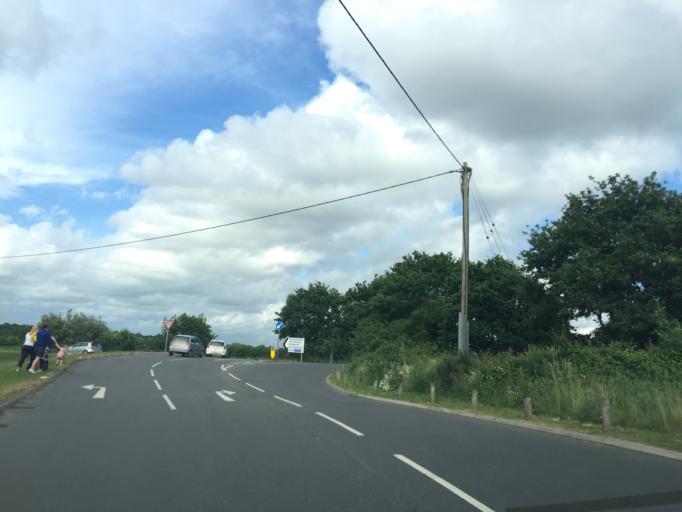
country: GB
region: England
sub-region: Hampshire
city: Cadnam
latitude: 50.9462
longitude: -1.5395
